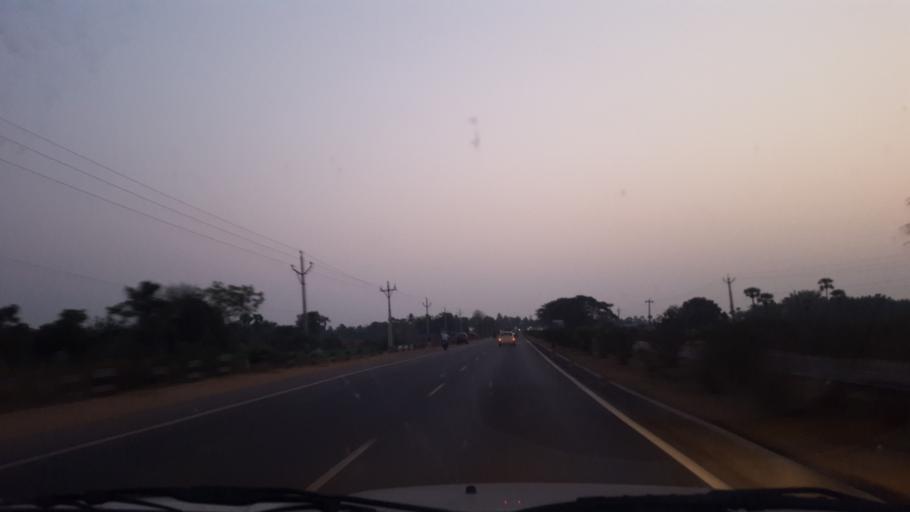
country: IN
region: Andhra Pradesh
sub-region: East Godavari
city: Peddapuram
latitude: 17.1527
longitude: 81.9877
